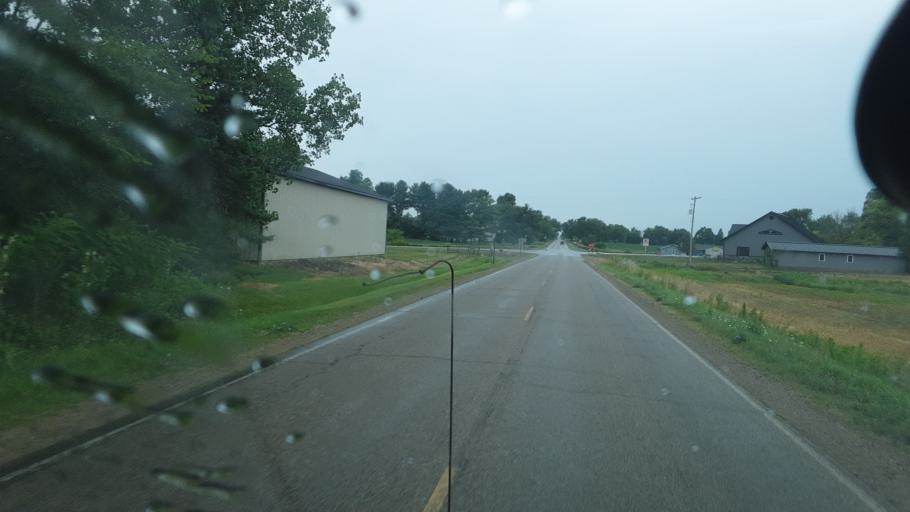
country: US
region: Michigan
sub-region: Hillsdale County
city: Reading
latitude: 41.7081
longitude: -84.7486
